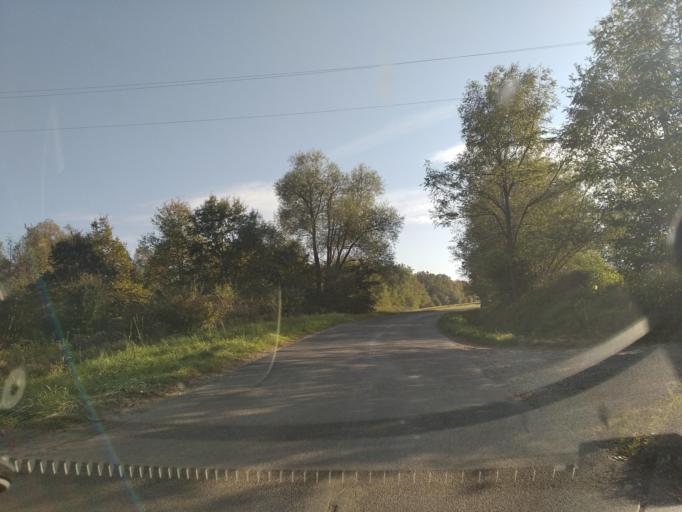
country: PL
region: Subcarpathian Voivodeship
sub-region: Powiat sanocki
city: Besko
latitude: 49.5829
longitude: 21.9521
